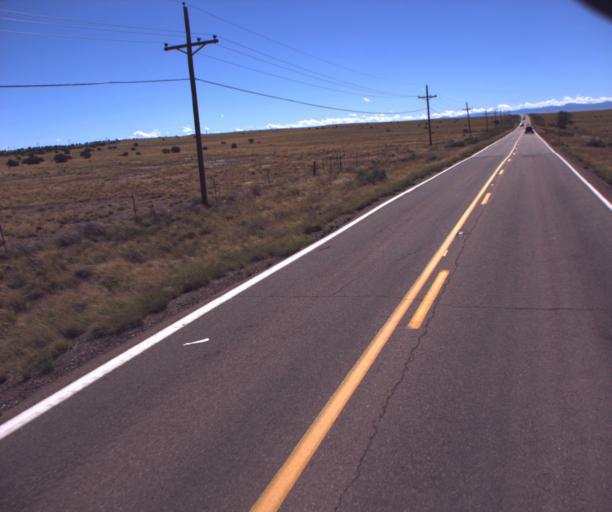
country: US
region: Arizona
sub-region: Apache County
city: Saint Johns
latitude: 34.5676
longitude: -109.3388
